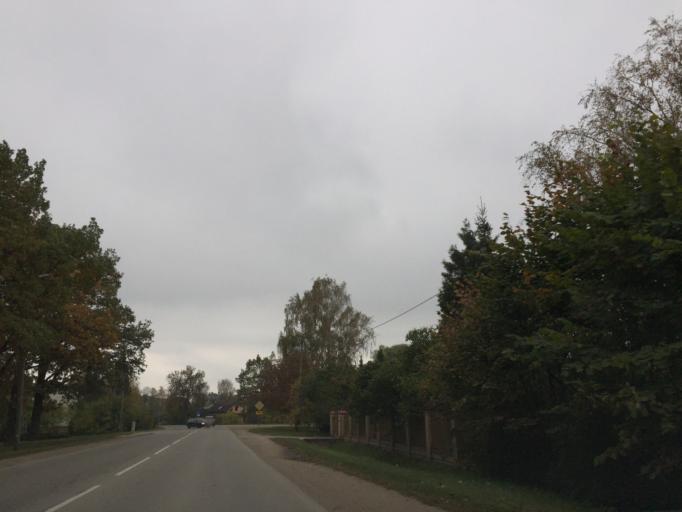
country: LV
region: Jelgava
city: Jelgava
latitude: 56.6605
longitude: 23.7384
